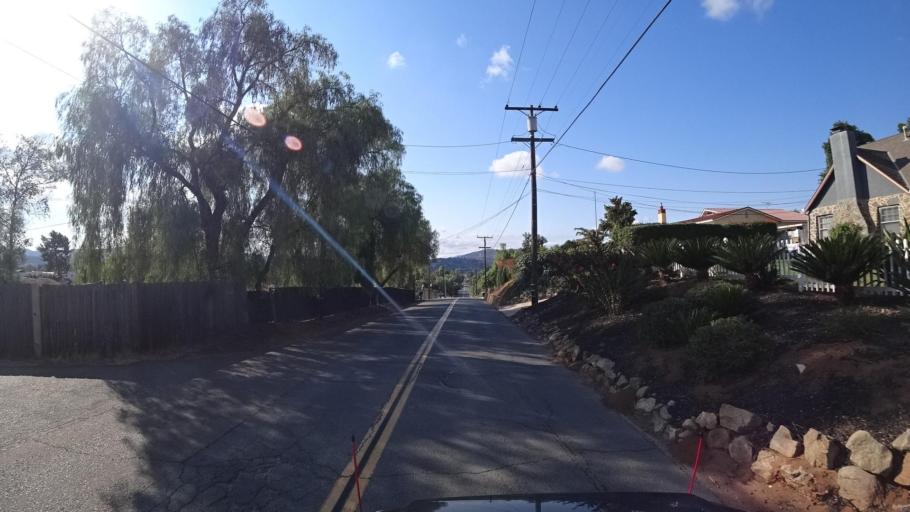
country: US
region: California
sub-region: San Diego County
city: Eucalyptus Hills
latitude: 32.8724
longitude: -116.9390
